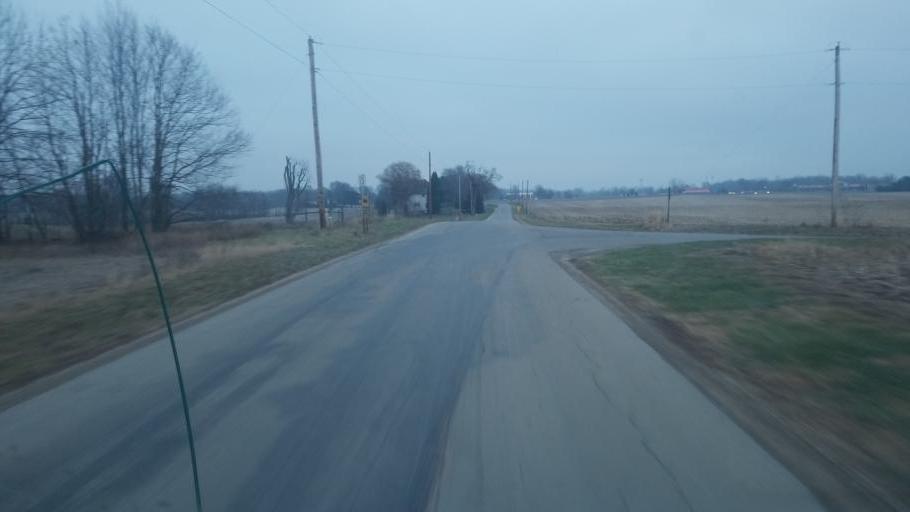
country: US
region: Ohio
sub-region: Seneca County
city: Tiffin
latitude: 40.9881
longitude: -83.1805
